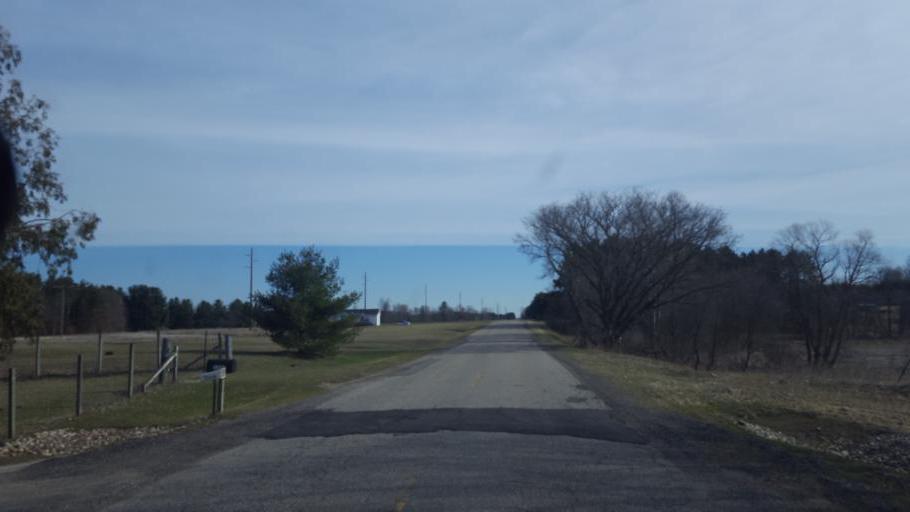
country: US
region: Michigan
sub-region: Mecosta County
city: Big Rapids
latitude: 43.5745
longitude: -85.5082
